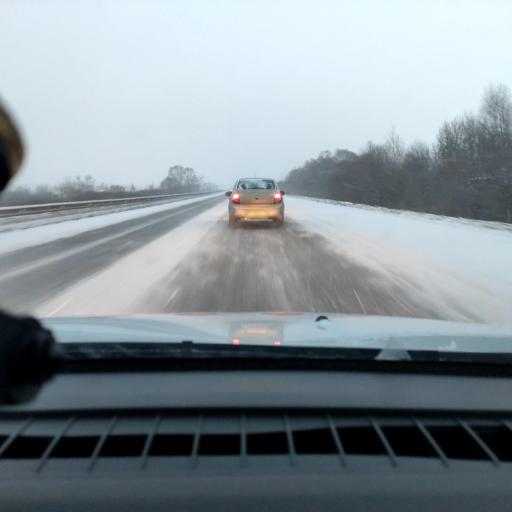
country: RU
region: Samara
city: Kinel'-Cherkassy
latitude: 53.4113
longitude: 51.4414
